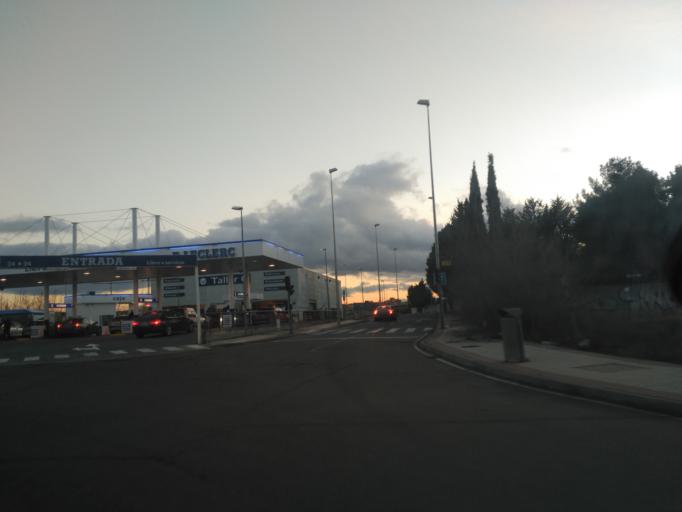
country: ES
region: Castille and Leon
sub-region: Provincia de Salamanca
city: Santa Marta de Tormes
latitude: 40.9455
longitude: -5.6398
